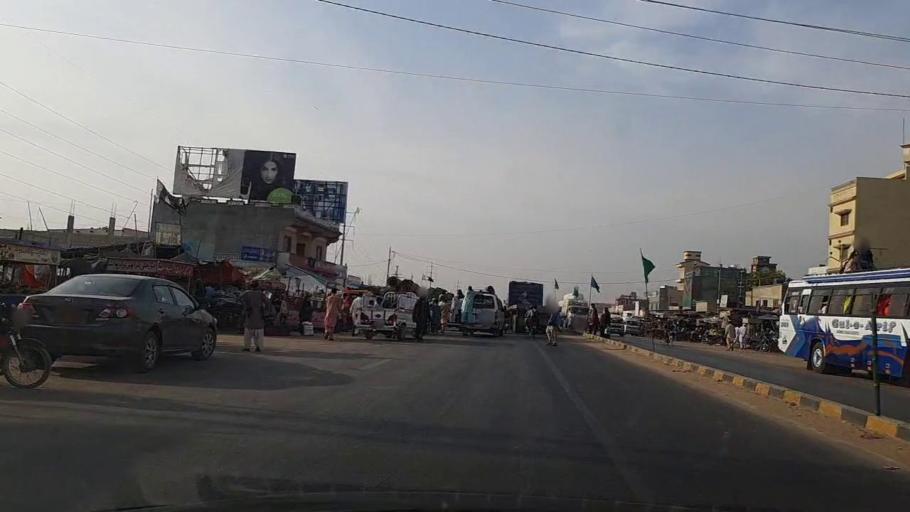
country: PK
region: Sindh
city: Gharo
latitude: 24.7910
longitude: 67.5253
